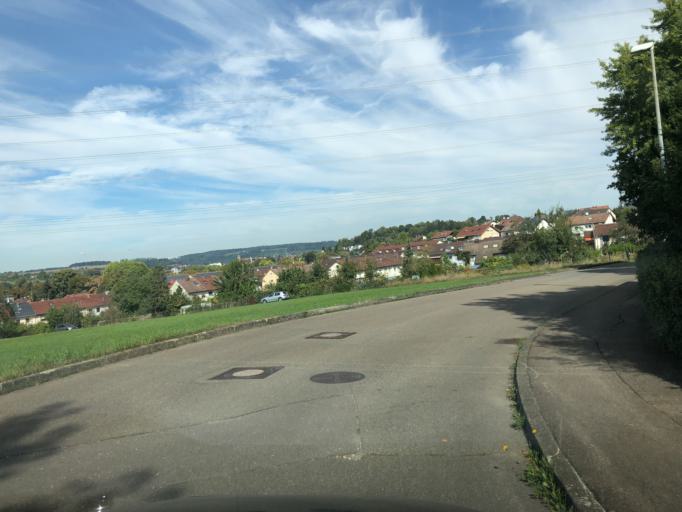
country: DE
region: Baden-Wuerttemberg
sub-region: Regierungsbezirk Stuttgart
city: Frickenhausen
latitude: 48.6100
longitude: 9.3542
